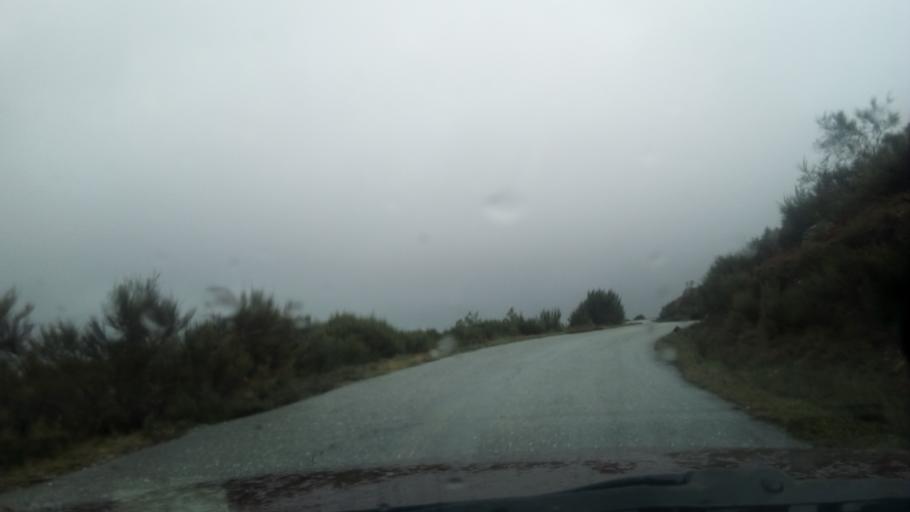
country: PT
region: Guarda
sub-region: Celorico da Beira
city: Celorico da Beira
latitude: 40.5254
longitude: -7.4529
